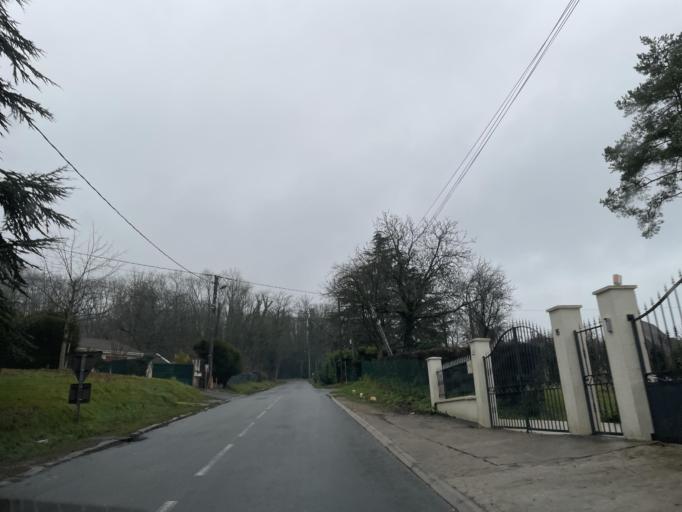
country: FR
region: Ile-de-France
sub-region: Departement de Seine-et-Marne
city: Pommeuse
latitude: 48.8194
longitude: 3.0104
